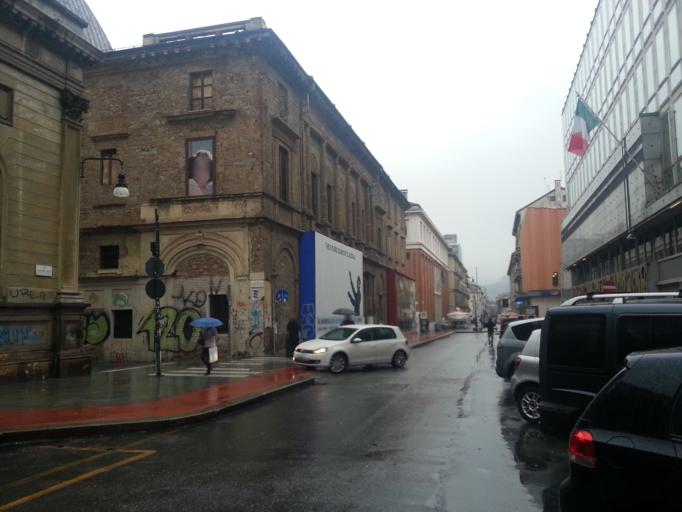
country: IT
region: Piedmont
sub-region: Provincia di Torino
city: Turin
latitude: 45.0686
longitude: 7.6915
